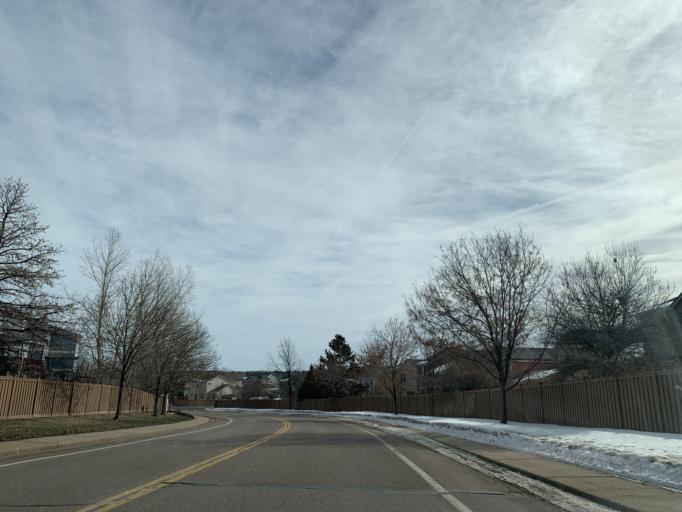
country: US
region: Colorado
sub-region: Douglas County
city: Carriage Club
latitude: 39.5369
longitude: -104.9315
